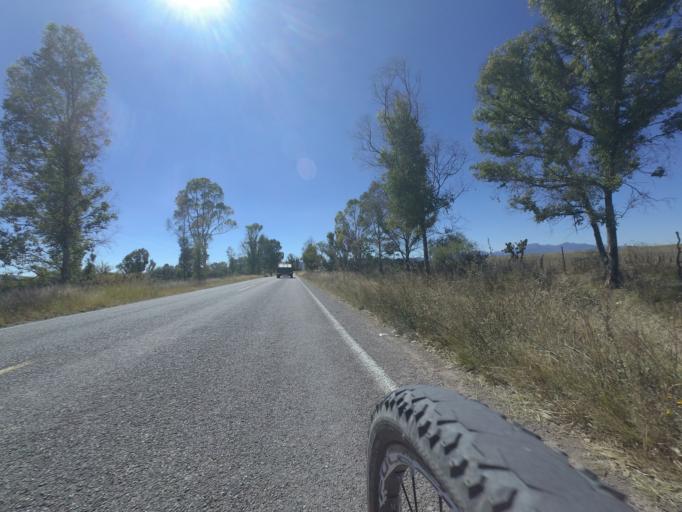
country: MX
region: Aguascalientes
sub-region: Aguascalientes
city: Los Canos
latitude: 21.8790
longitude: -102.4938
